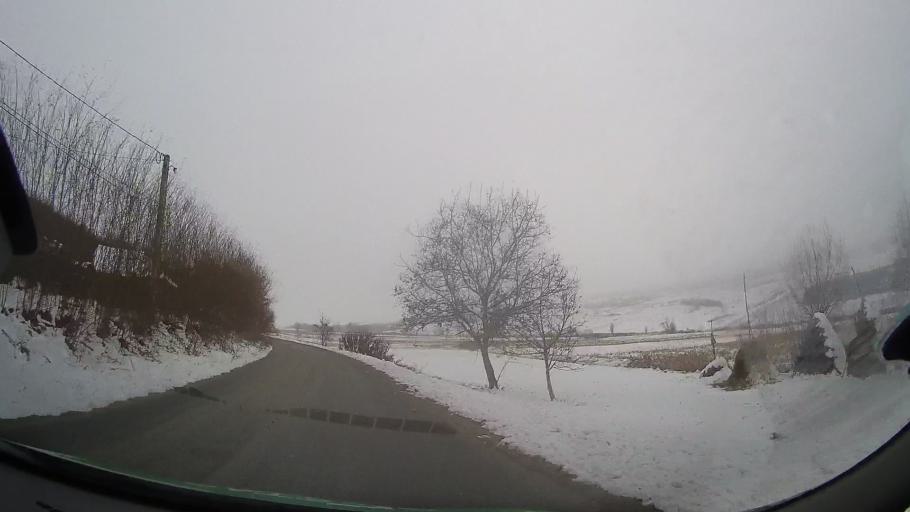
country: RO
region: Bacau
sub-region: Comuna Vultureni
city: Vultureni
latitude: 46.3386
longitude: 27.2905
